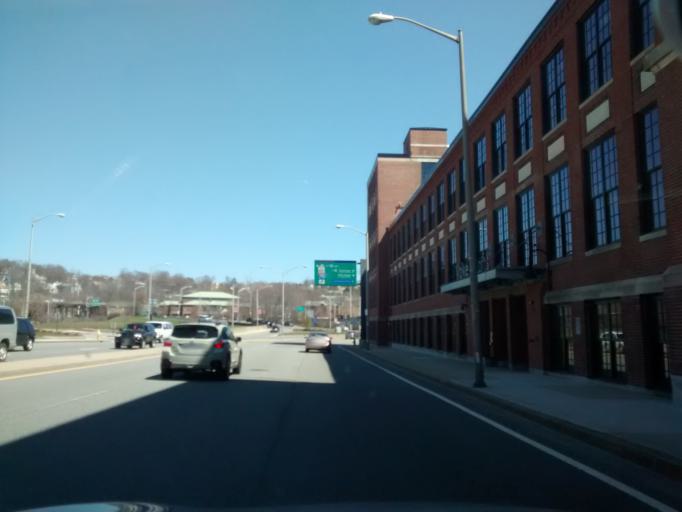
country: US
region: Massachusetts
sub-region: Worcester County
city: Worcester
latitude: 42.2733
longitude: -71.7998
